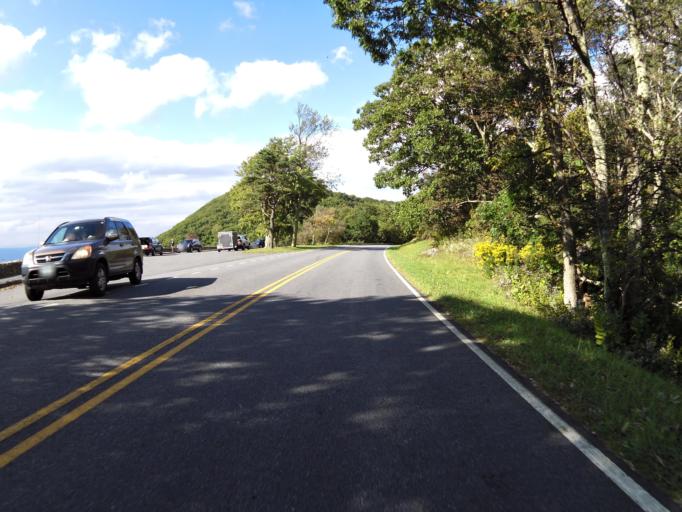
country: US
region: Virginia
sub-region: Page County
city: Luray
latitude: 38.5743
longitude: -78.3839
